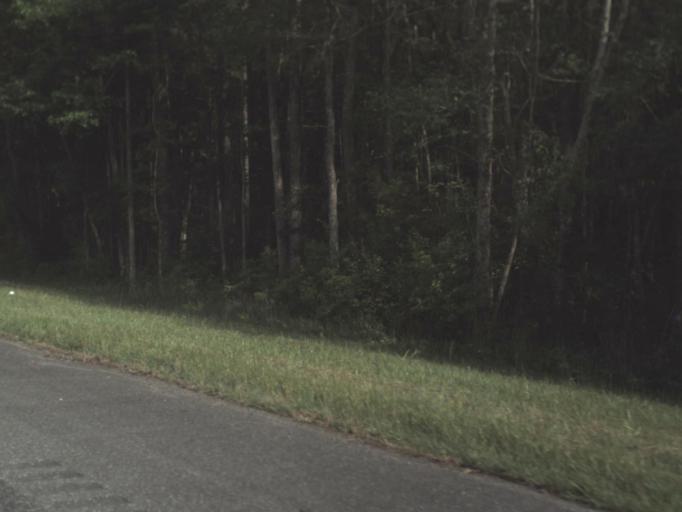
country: US
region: Florida
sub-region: Columbia County
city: Watertown
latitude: 30.2538
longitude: -82.4128
